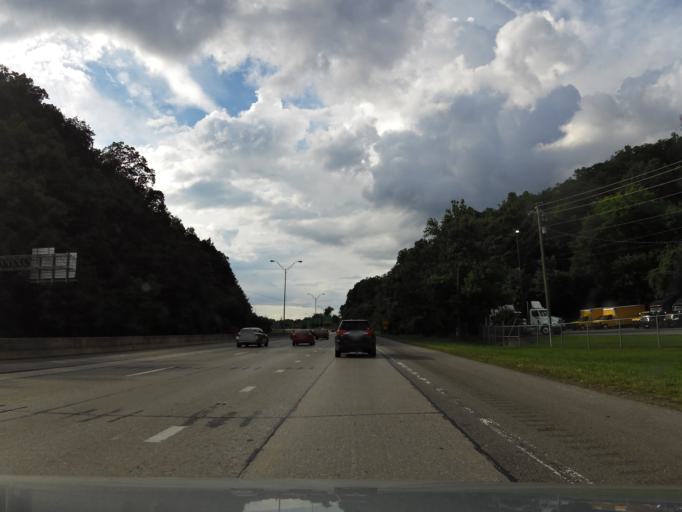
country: US
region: Tennessee
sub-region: Knox County
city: Knoxville
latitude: 35.9950
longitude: -83.9529
